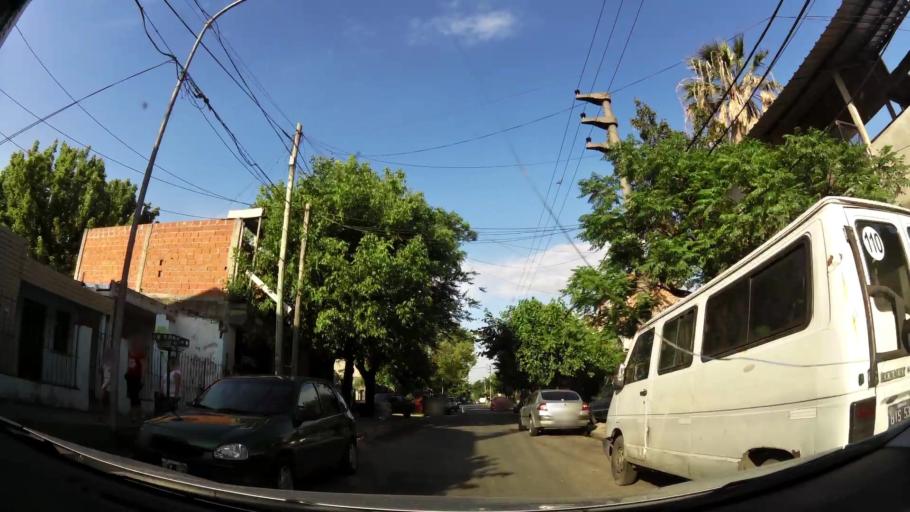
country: AR
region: Buenos Aires
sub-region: Partido de Tigre
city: Tigre
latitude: -34.4673
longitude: -58.6618
